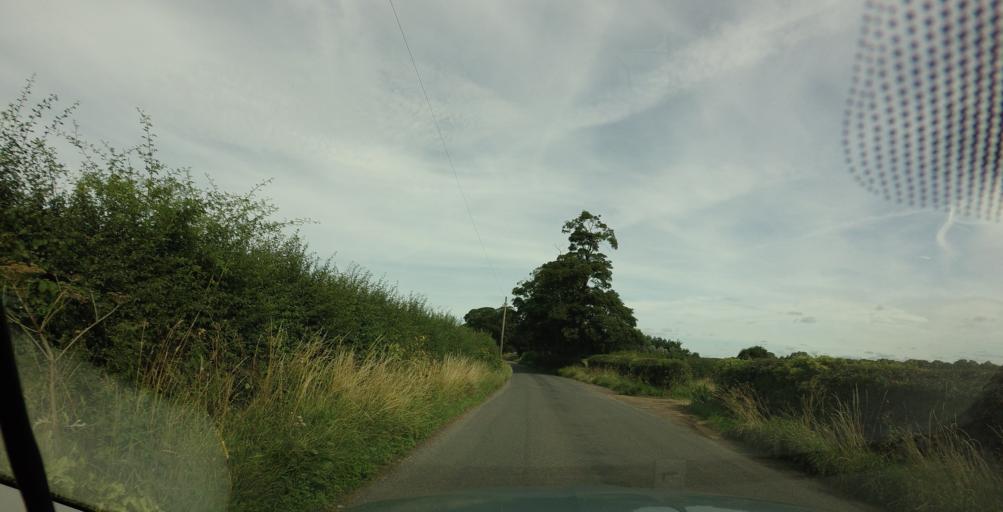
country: GB
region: England
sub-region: North Yorkshire
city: Ripon
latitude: 54.1095
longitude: -1.5165
